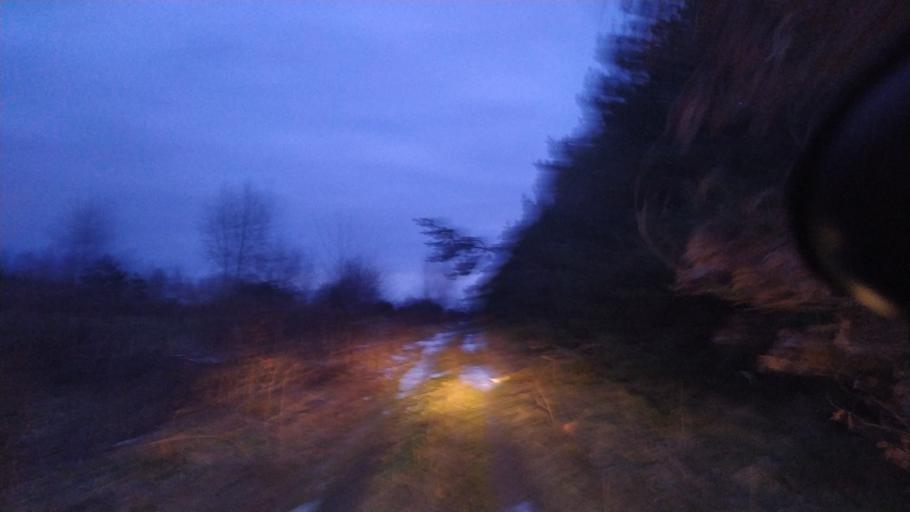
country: PL
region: Lublin Voivodeship
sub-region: Powiat lubelski
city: Jastkow
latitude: 51.3859
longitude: 22.4358
